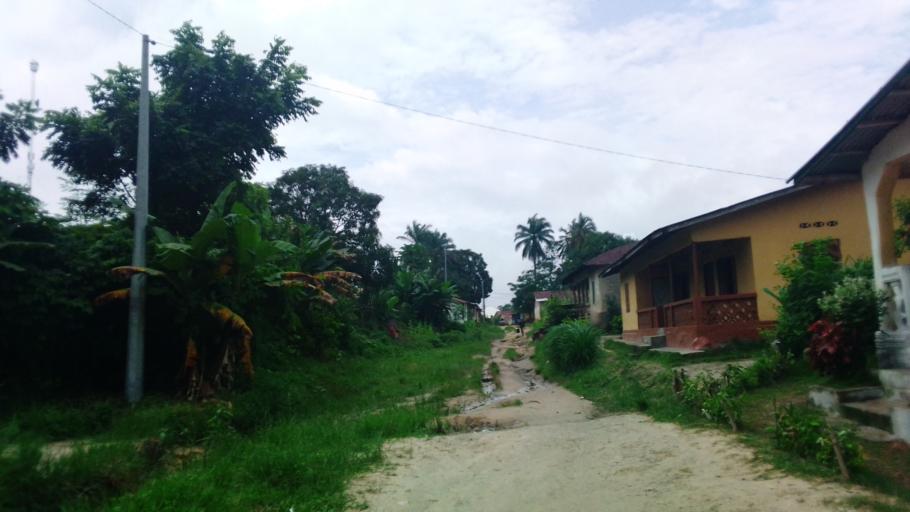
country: SL
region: Northern Province
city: Lunsar
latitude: 8.6851
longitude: -12.5395
